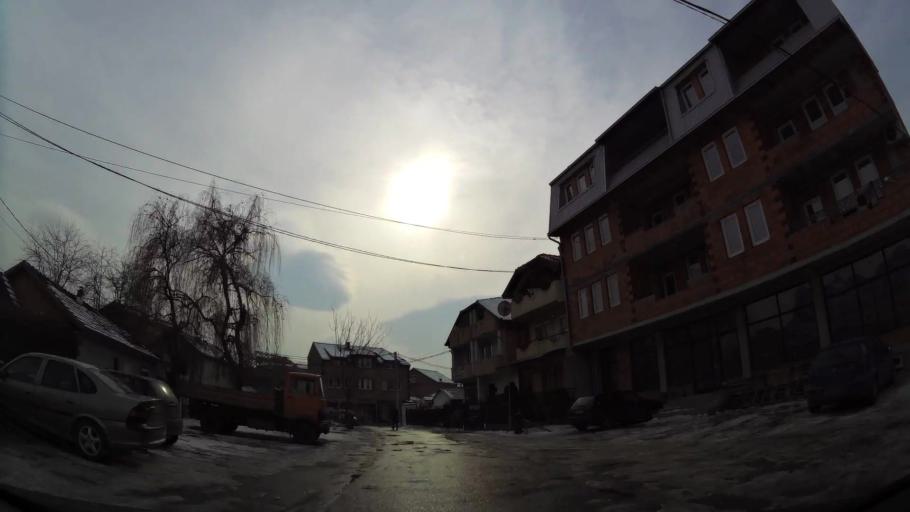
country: MK
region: Cair
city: Cair
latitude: 42.0111
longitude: 21.4371
